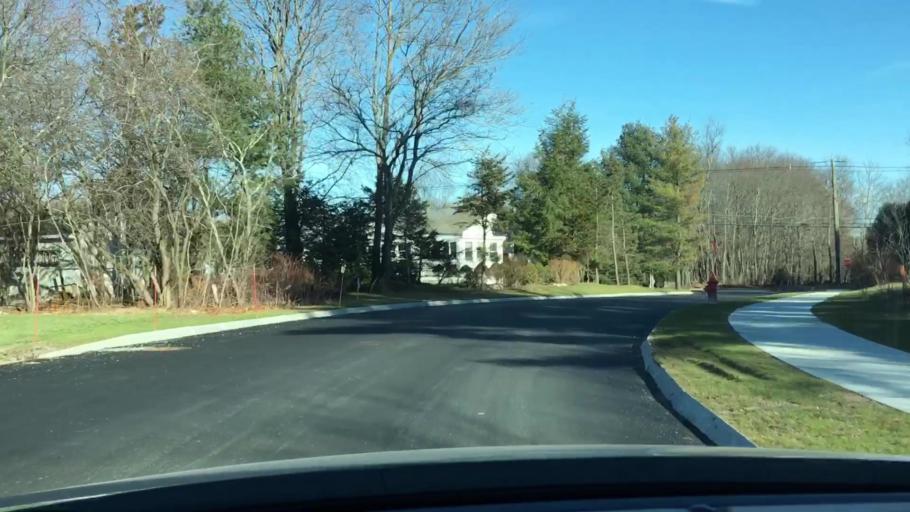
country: US
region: Massachusetts
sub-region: Norfolk County
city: Walpole
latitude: 42.1741
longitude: -71.2434
